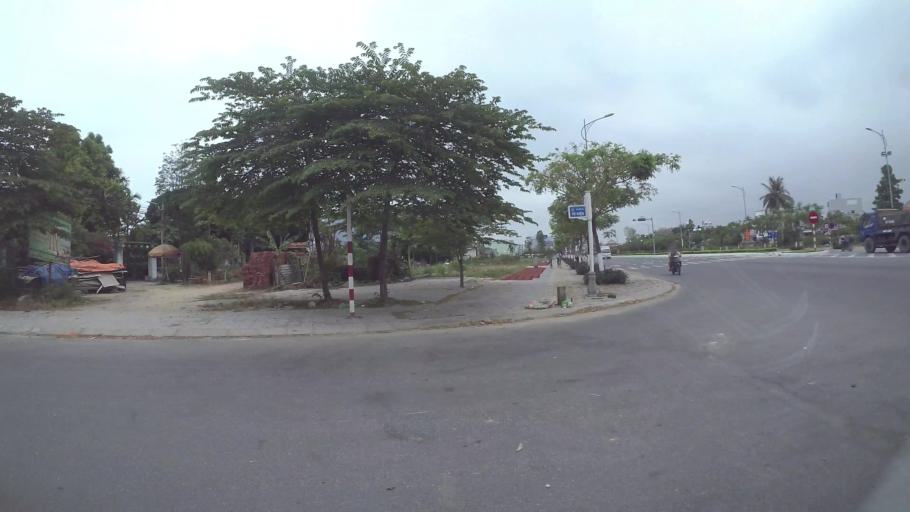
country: VN
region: Da Nang
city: Lien Chieu
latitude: 16.0698
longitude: 108.1671
